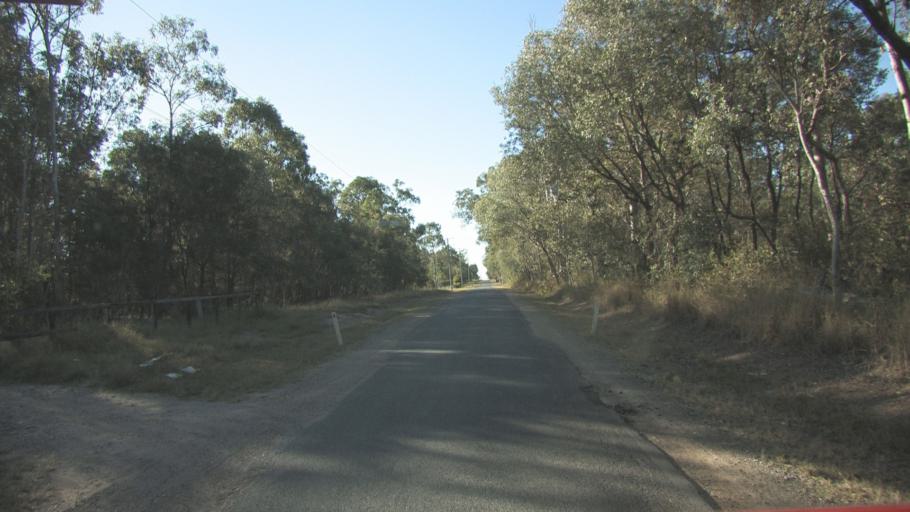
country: AU
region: Queensland
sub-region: Logan
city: North Maclean
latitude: -27.7872
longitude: 153.0387
